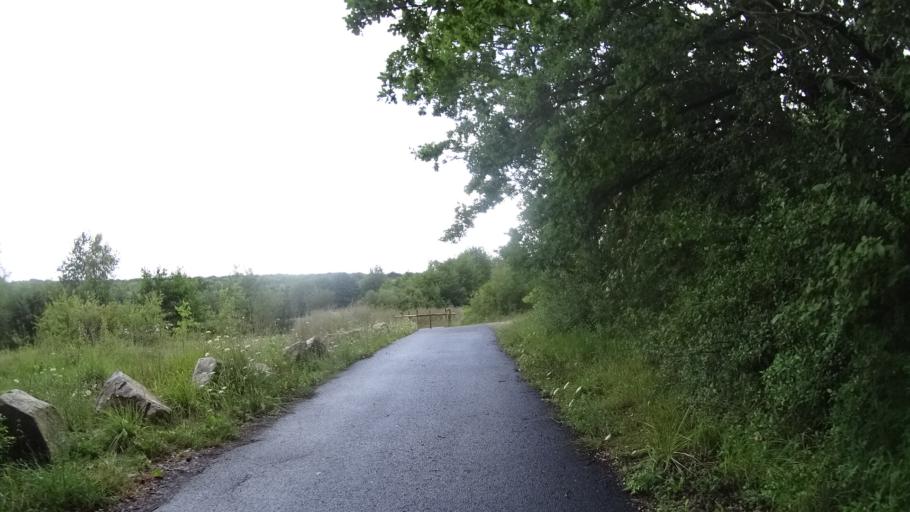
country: FR
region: Lorraine
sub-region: Departement de la Moselle
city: Lorquin
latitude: 48.6847
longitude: 6.8368
